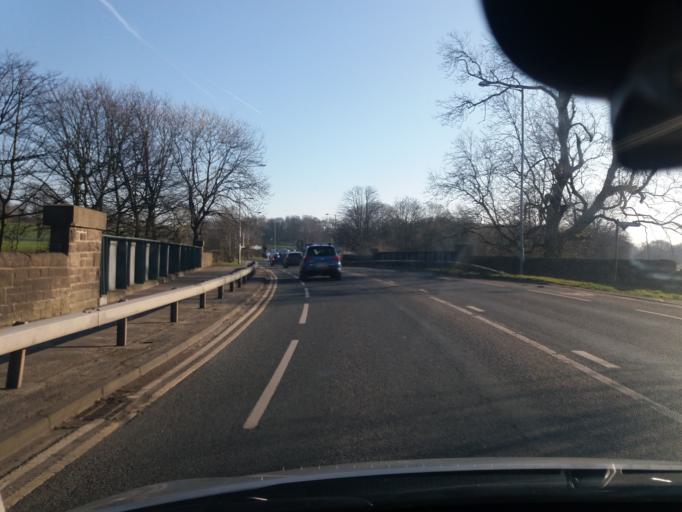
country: GB
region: England
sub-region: Lancashire
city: Adlington
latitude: 53.6304
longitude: -2.6112
